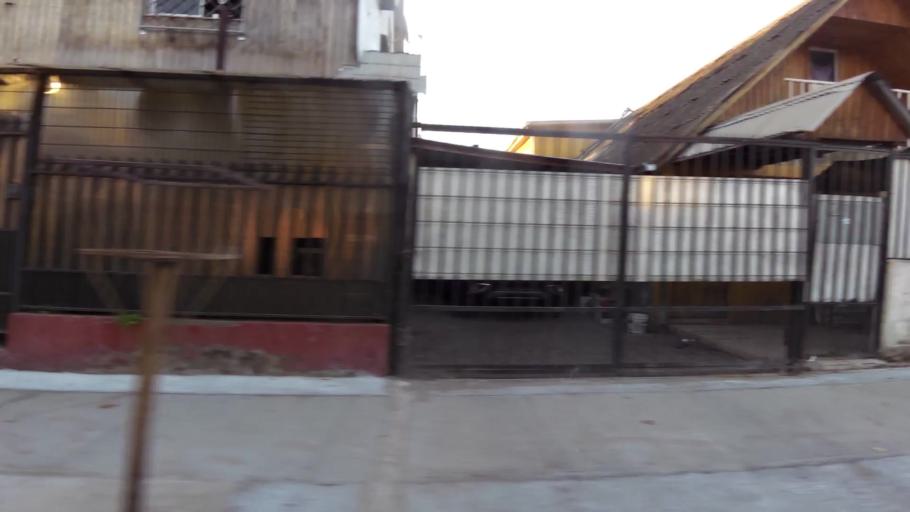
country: CL
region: Maule
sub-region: Provincia de Talca
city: Talca
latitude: -35.4438
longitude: -71.6380
